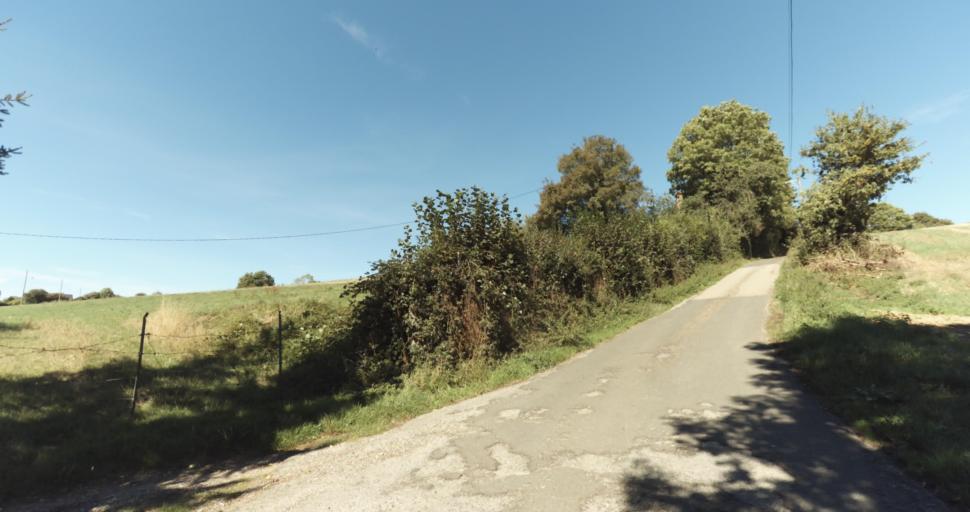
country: FR
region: Lower Normandy
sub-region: Departement de l'Orne
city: Gace
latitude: 48.7878
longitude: 0.2646
